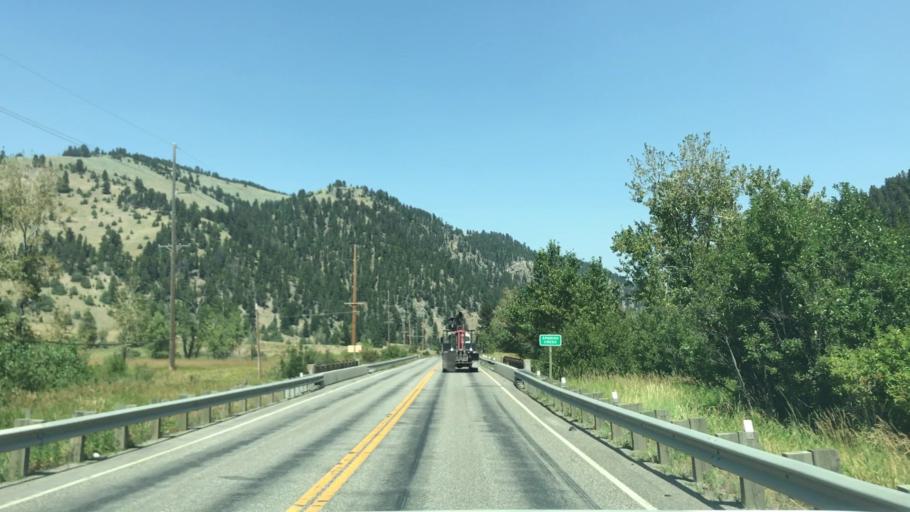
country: US
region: Montana
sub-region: Gallatin County
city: Four Corners
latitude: 45.4935
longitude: -111.2722
